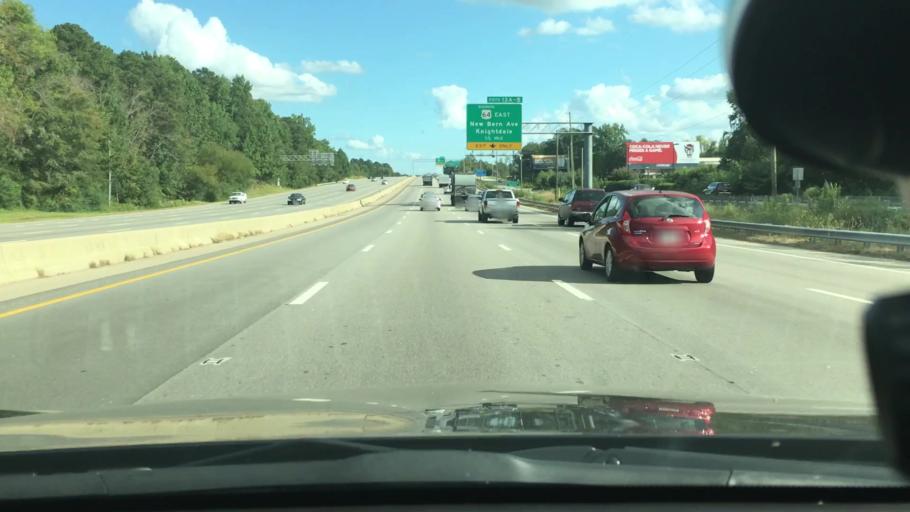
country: US
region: North Carolina
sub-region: Wake County
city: Raleigh
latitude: 35.7997
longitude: -78.5903
